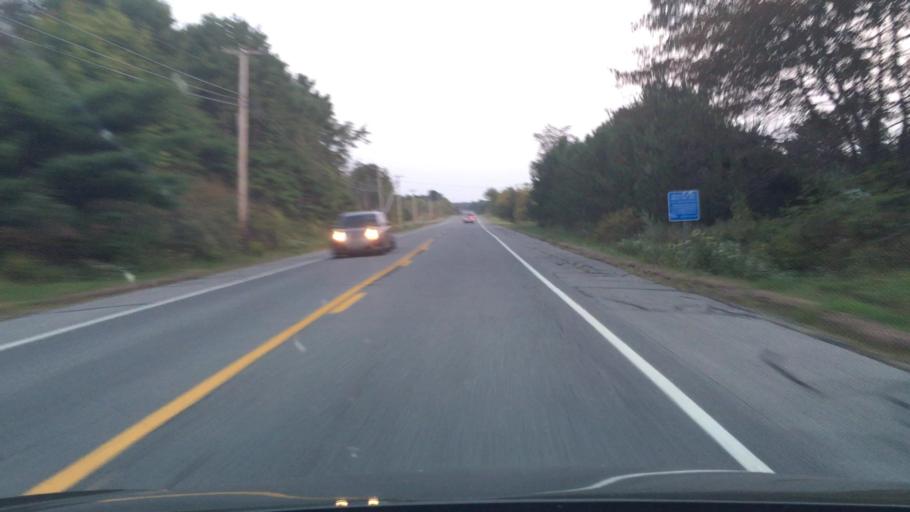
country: US
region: Maine
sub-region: Waldo County
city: Stockton Springs
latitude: 44.5361
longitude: -68.8611
